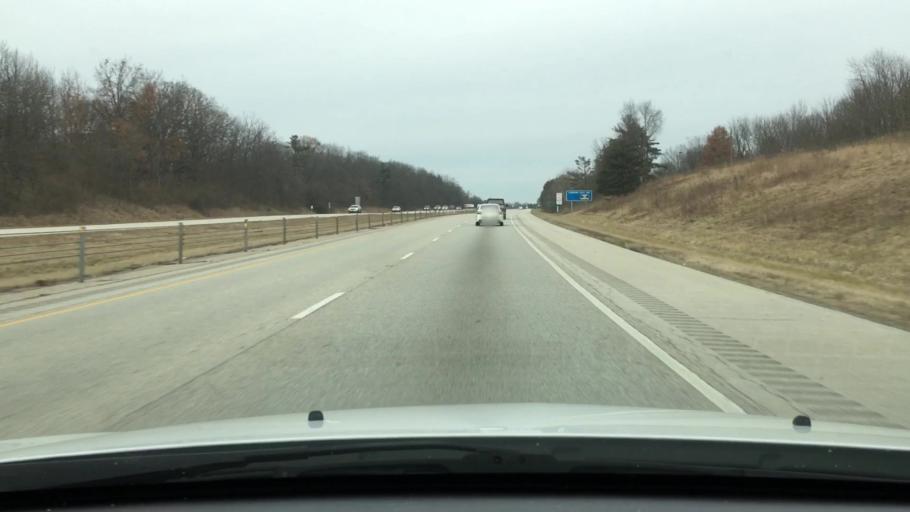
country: US
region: Illinois
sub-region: Sangamon County
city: Sherman
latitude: 39.8788
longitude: -89.5966
